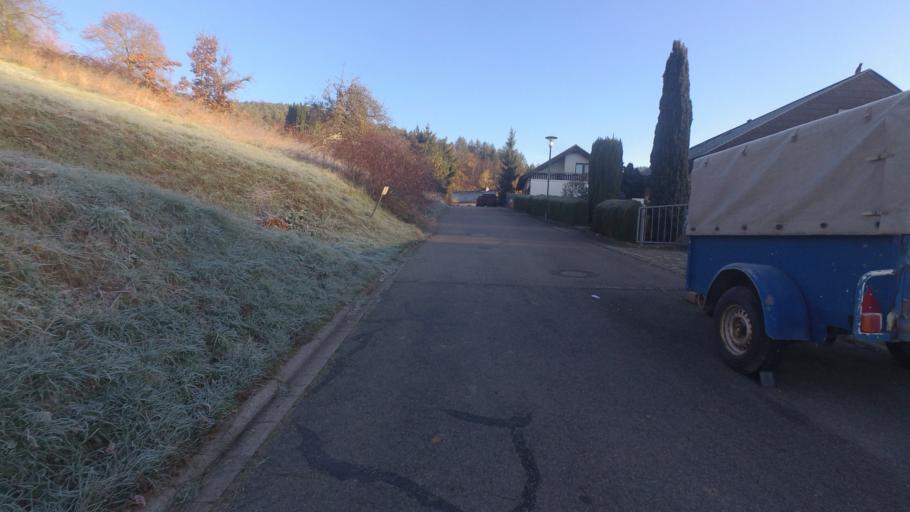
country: DE
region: Baden-Wuerttemberg
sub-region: Karlsruhe Region
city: Heiligkreuzsteinach
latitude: 49.4885
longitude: 8.8003
